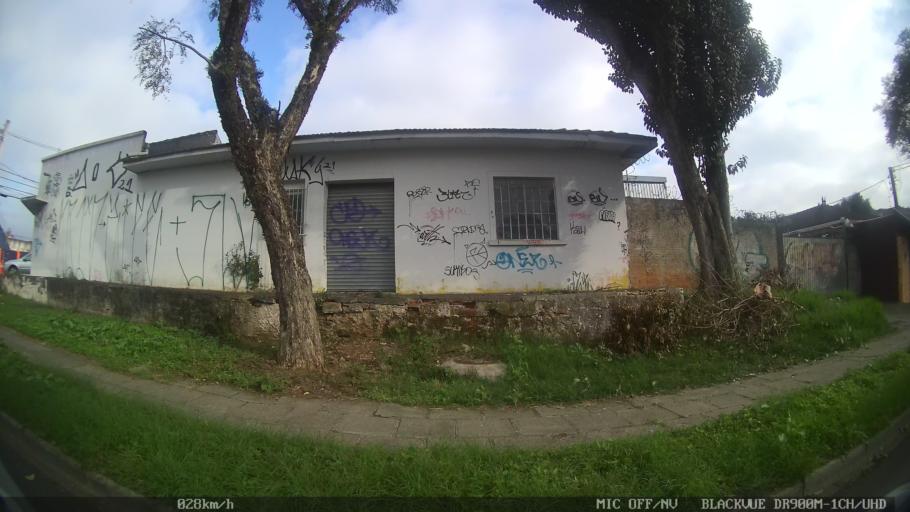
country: BR
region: Parana
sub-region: Curitiba
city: Curitiba
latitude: -25.3988
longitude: -49.3389
